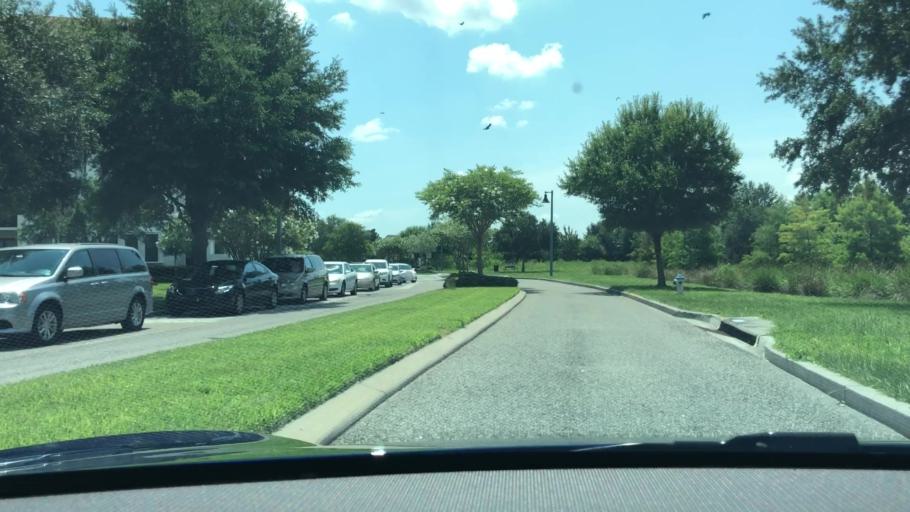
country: US
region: Florida
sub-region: Orange County
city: Winter Park
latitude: 28.5779
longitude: -81.3216
